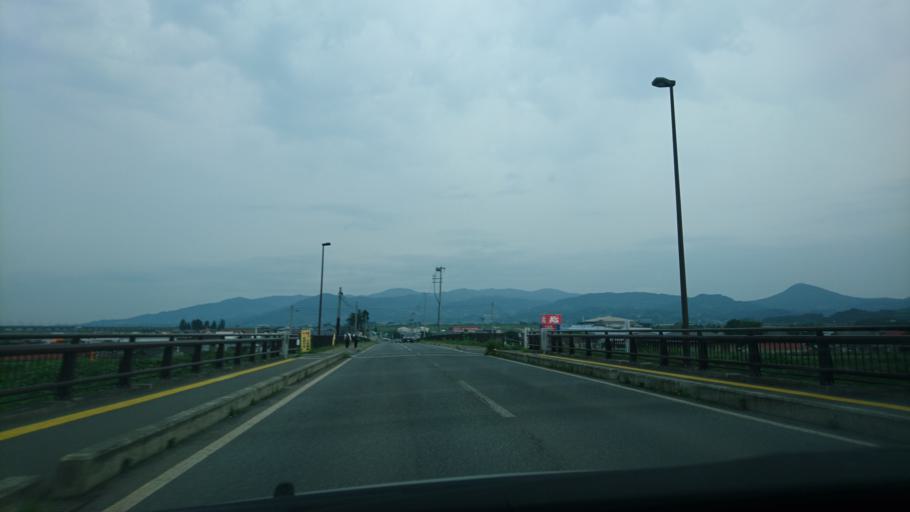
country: JP
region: Iwate
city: Ichinoseki
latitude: 38.9354
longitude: 141.1496
